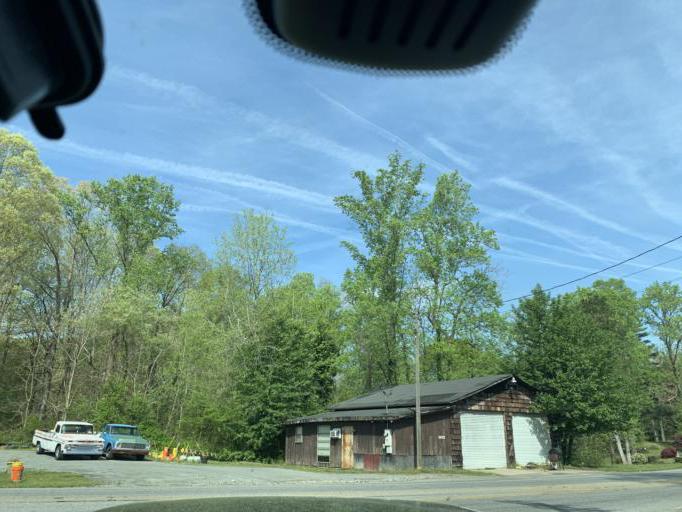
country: US
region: Georgia
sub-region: Forsyth County
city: Cumming
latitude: 34.2327
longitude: -84.0848
